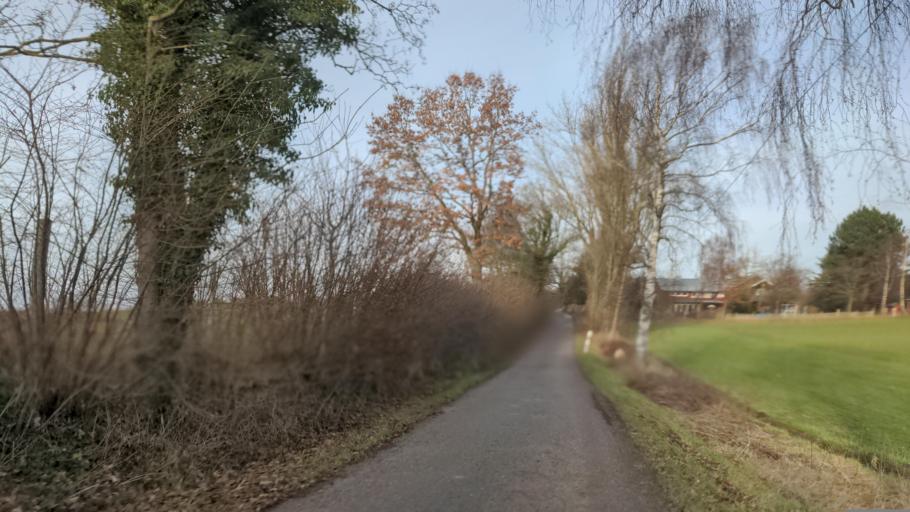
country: DE
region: Schleswig-Holstein
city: Eutin
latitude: 54.1688
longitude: 10.6263
